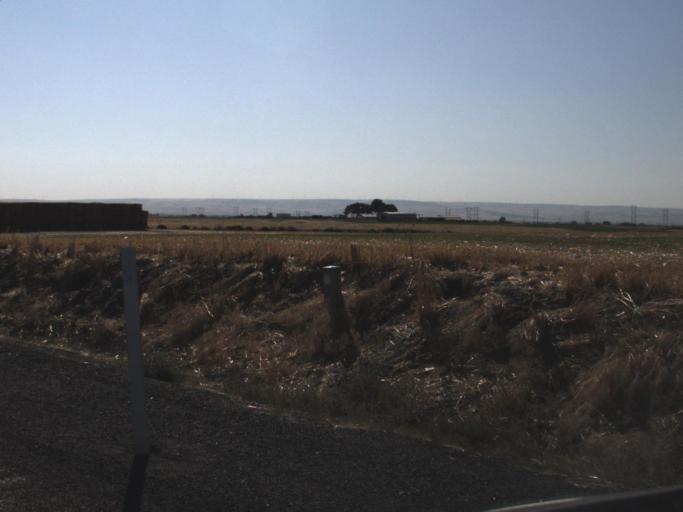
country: US
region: Washington
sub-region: Walla Walla County
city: Walla Walla
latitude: 46.0871
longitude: -118.3674
